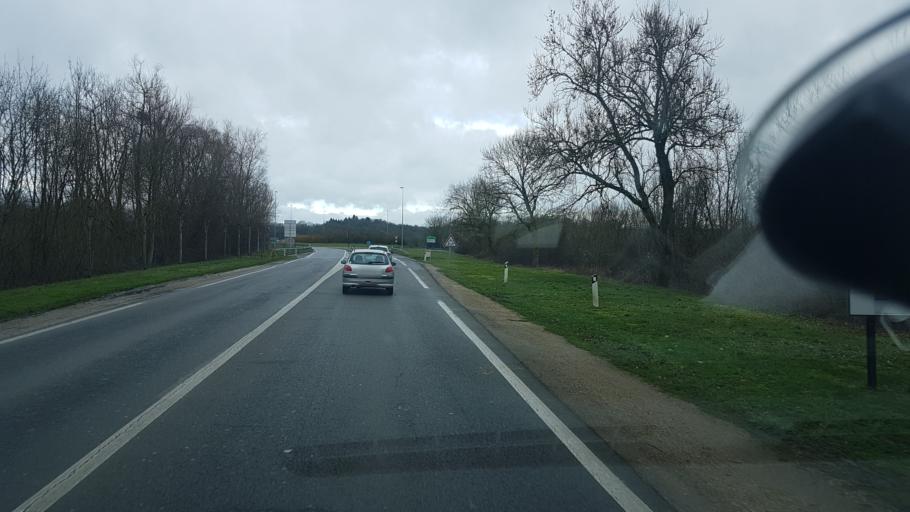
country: FR
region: Centre
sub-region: Departement du Loiret
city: Dordives
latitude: 48.1528
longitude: 2.7639
